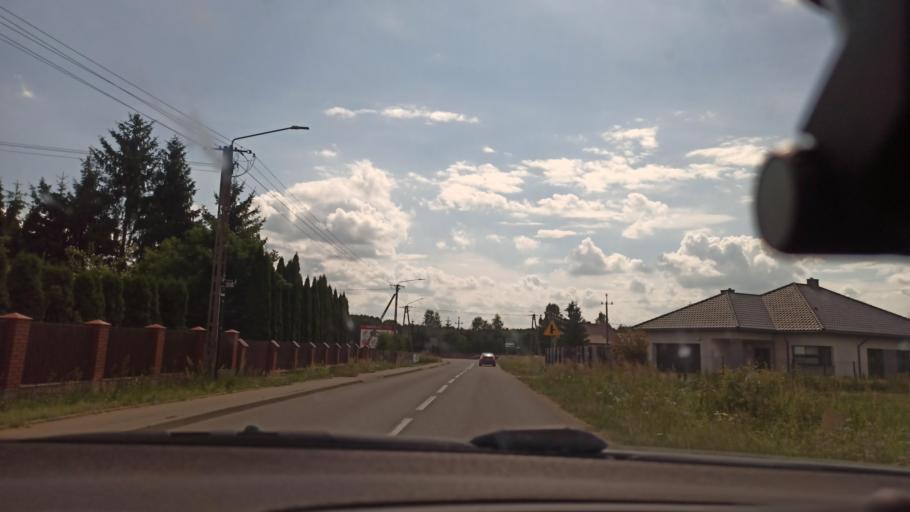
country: PL
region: Podlasie
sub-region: Powiat bialostocki
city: Turosn Koscielna
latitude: 53.0651
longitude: 23.0971
